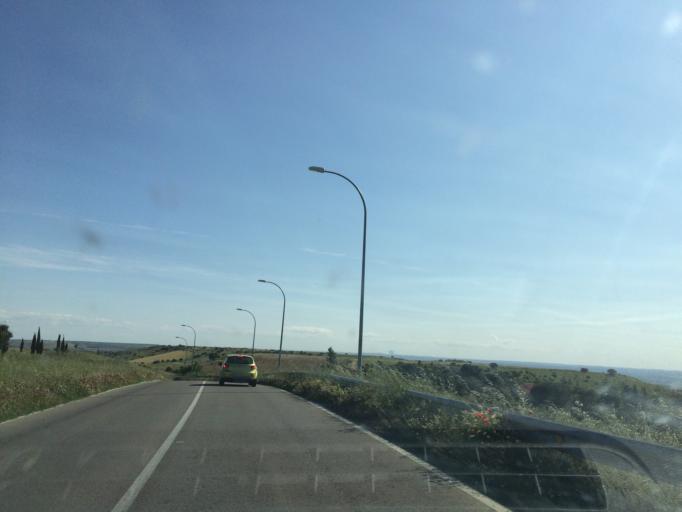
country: ES
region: Madrid
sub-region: Provincia de Madrid
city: Ribatejada
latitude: 40.6953
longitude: -3.4387
